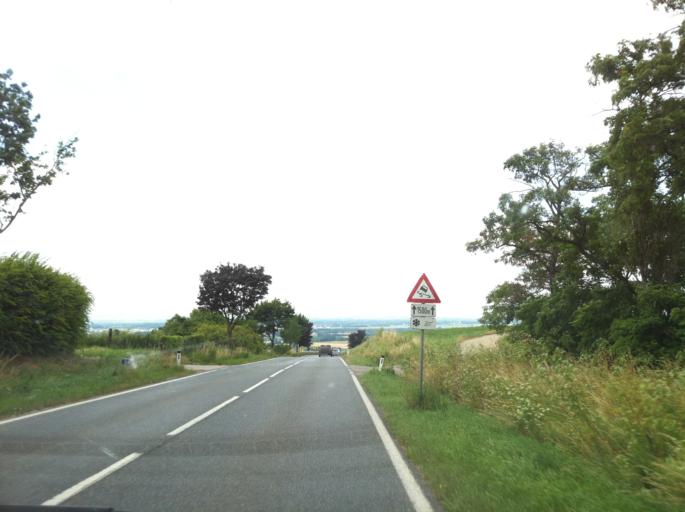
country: AT
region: Lower Austria
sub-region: Politischer Bezirk Tulln
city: Tulln
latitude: 48.2768
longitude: 16.0714
